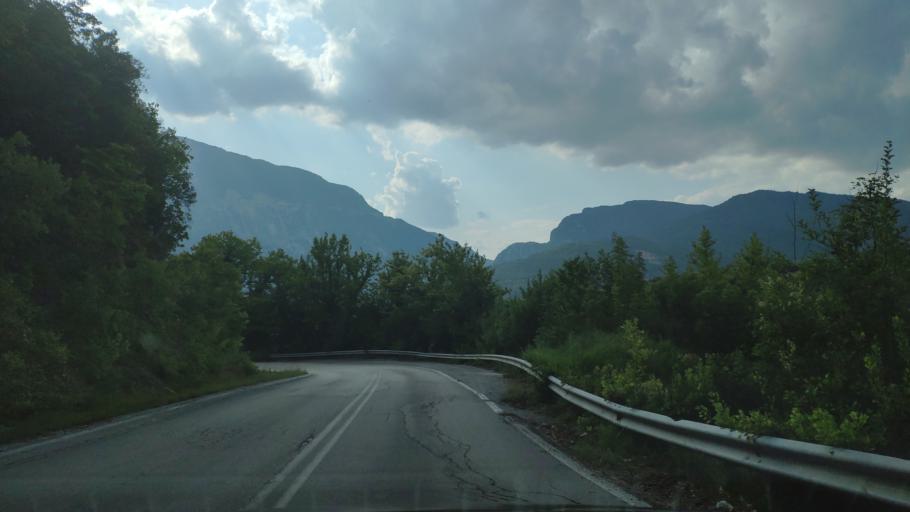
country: GR
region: Epirus
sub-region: Nomos Artas
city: Agios Dimitrios
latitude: 39.4570
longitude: 21.0496
